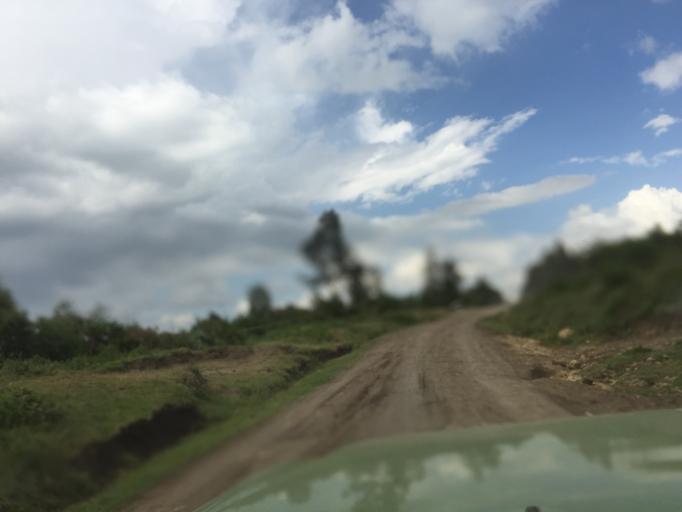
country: KE
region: Nyandarua
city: Ol Kalou
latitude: -0.4687
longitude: 36.4102
